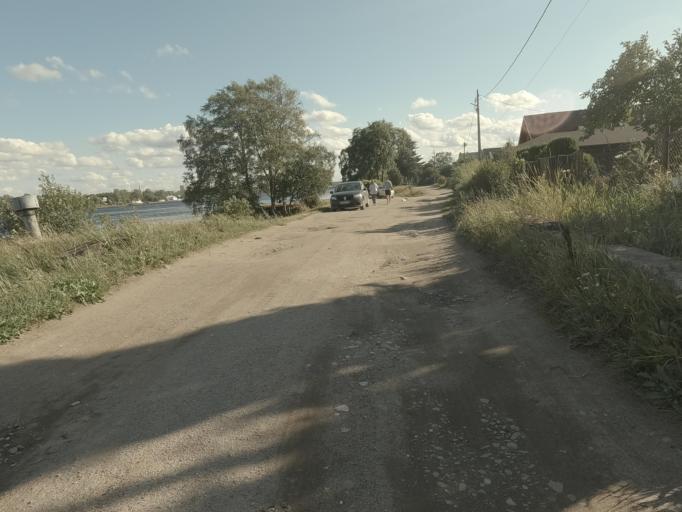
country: RU
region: Leningrad
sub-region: Volosovskiy Rayon
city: Shlissel'burg
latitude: 59.9557
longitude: 31.0281
